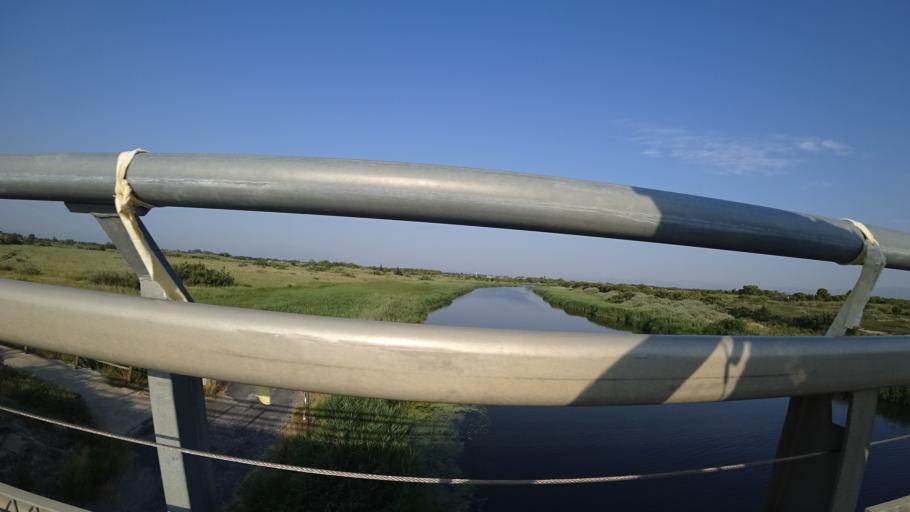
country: FR
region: Languedoc-Roussillon
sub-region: Departement des Pyrenees-Orientales
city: Torreilles
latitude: 42.7523
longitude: 3.0214
